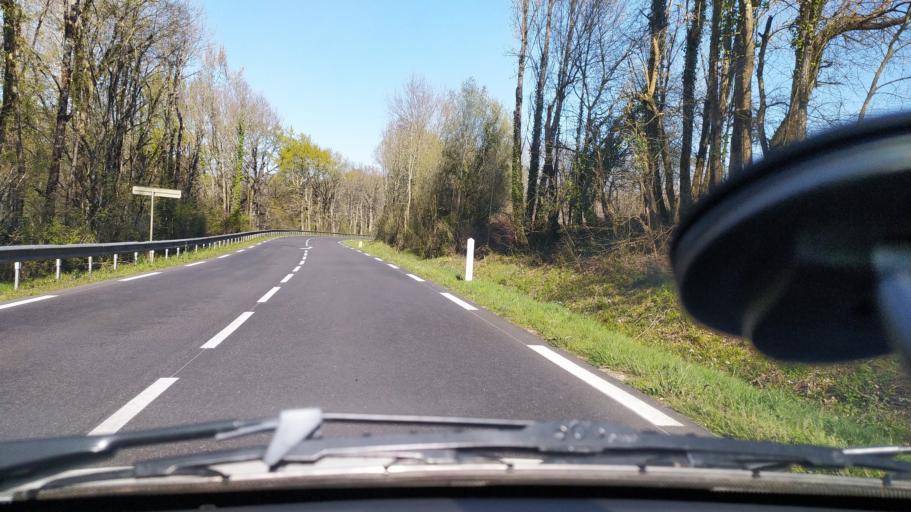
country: FR
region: Midi-Pyrenees
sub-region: Departement du Gers
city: Nogaro
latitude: 43.7484
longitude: -0.0599
